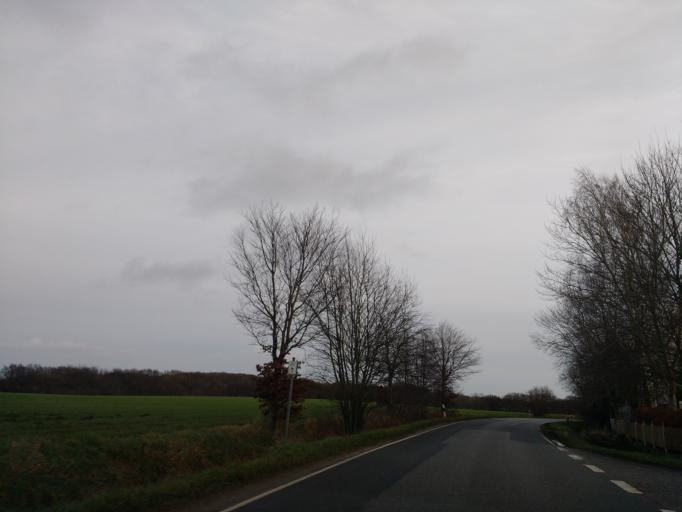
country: DE
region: Schleswig-Holstein
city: Susel
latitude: 54.0126
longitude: 10.6706
